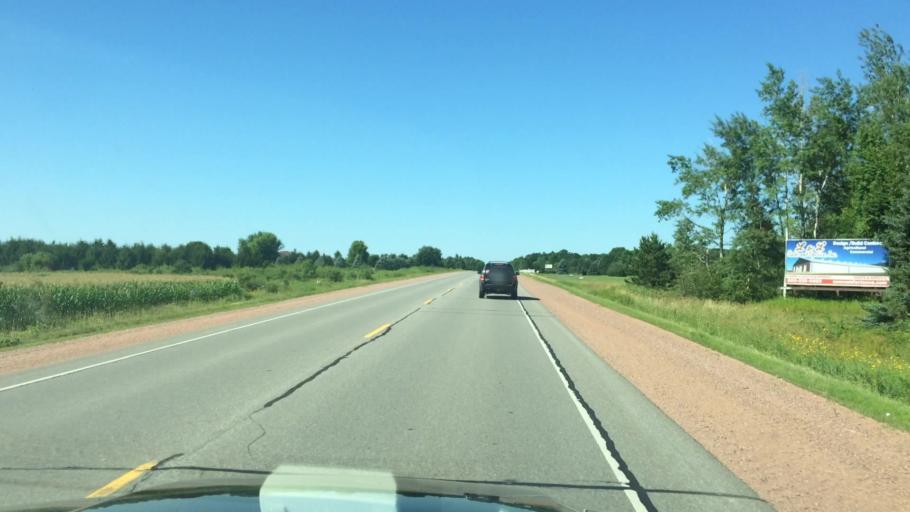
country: US
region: Wisconsin
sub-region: Wood County
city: Marshfield
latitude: 44.7196
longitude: -90.1037
